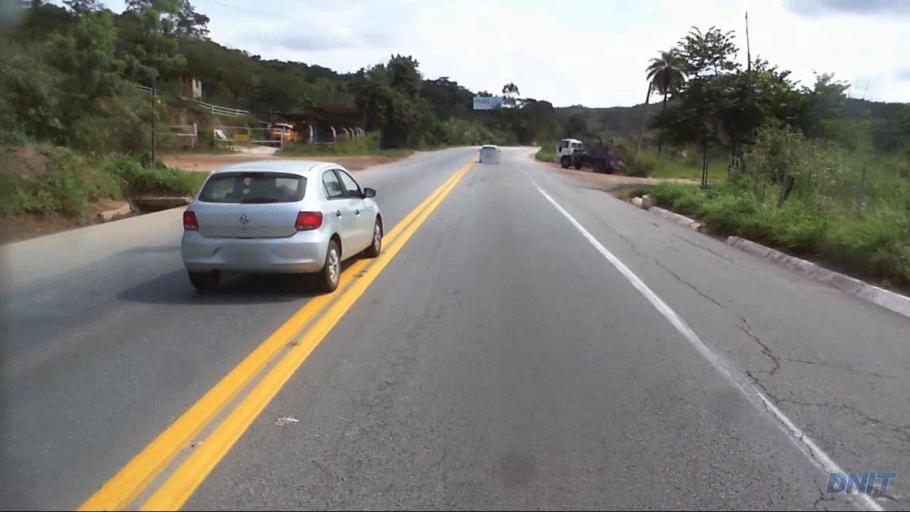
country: BR
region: Minas Gerais
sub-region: Santa Luzia
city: Santa Luzia
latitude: -19.8160
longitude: -43.8041
